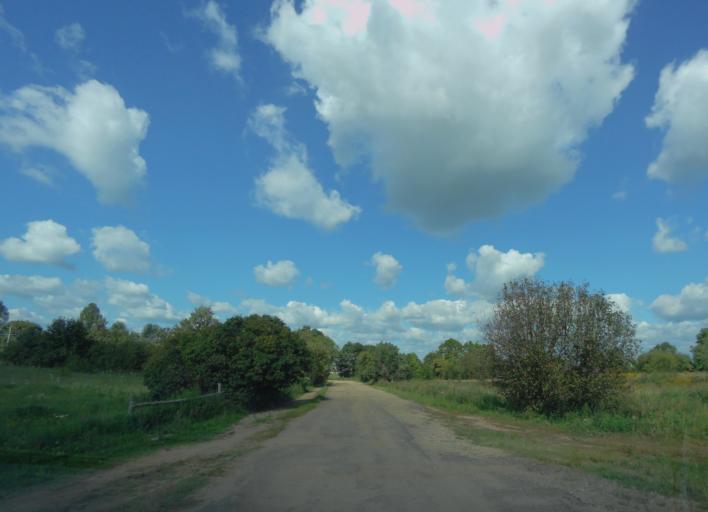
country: BY
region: Minsk
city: Zyembin
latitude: 54.4085
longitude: 28.3886
